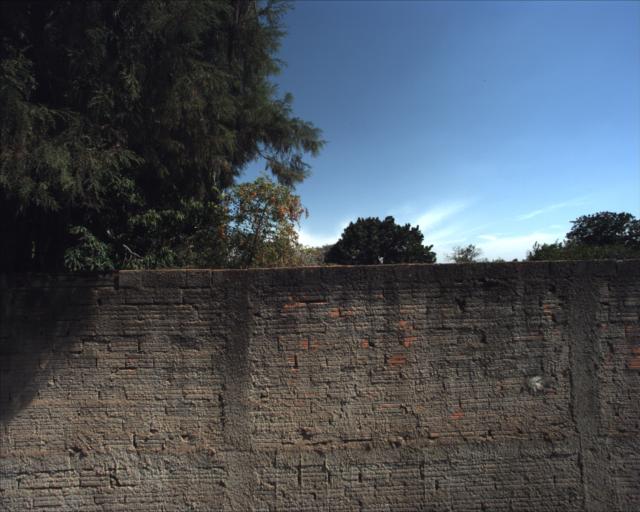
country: BR
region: Sao Paulo
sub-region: Aracoiaba Da Serra
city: Aracoiaba da Serra
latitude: -23.4881
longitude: -47.5470
